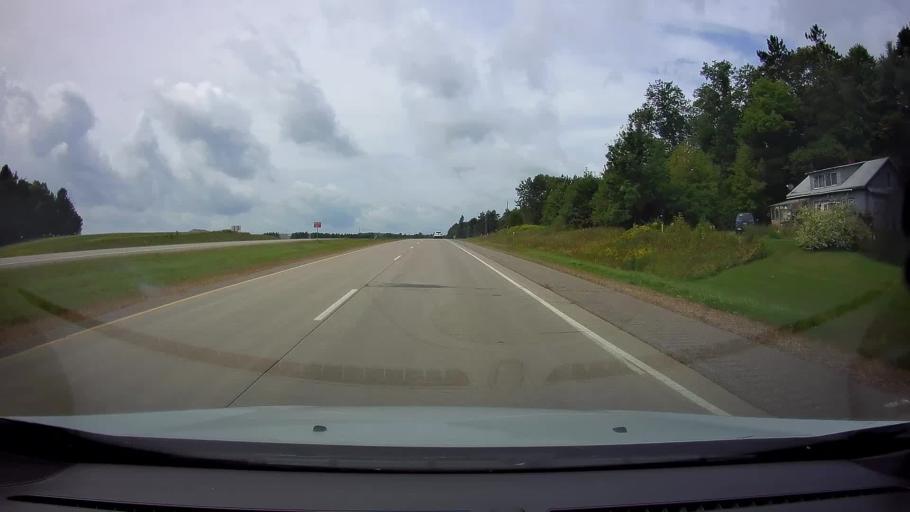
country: US
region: Wisconsin
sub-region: Shawano County
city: Wittenberg
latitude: 44.8039
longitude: -89.0202
